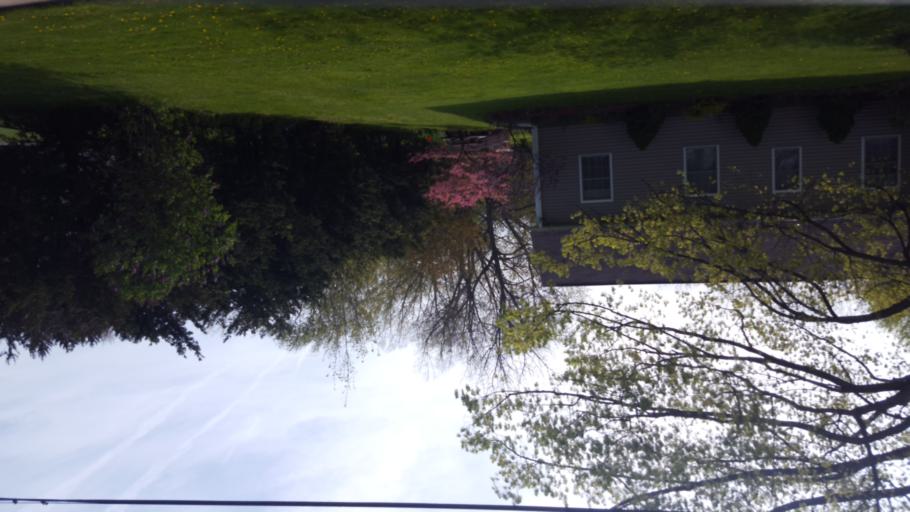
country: US
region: Ohio
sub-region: Lake County
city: Perry
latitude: 41.7973
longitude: -81.1045
